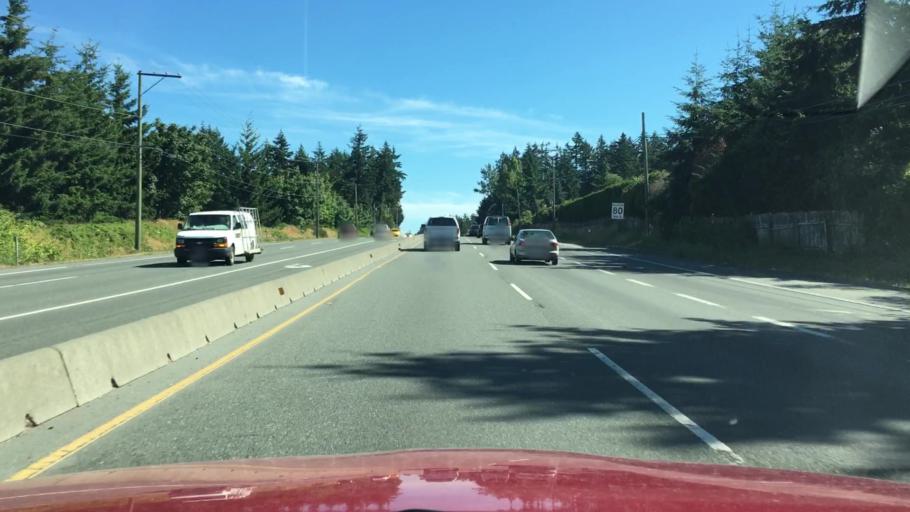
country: CA
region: British Columbia
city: North Saanich
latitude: 48.5532
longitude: -123.3927
